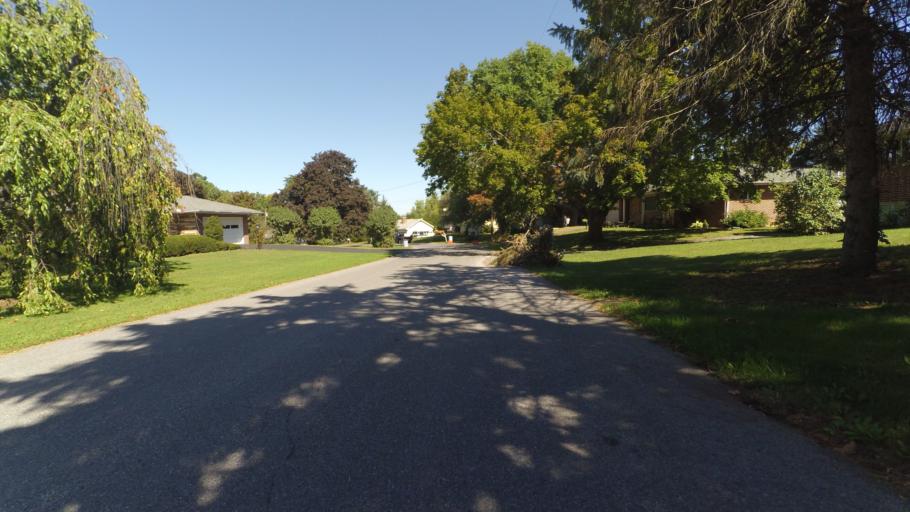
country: US
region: Pennsylvania
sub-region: Centre County
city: State College
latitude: 40.7708
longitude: -77.8889
